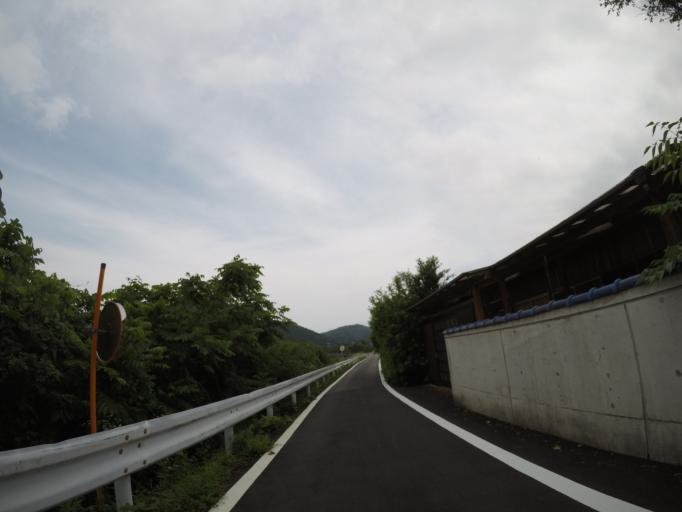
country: JP
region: Shizuoka
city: Fujinomiya
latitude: 35.2310
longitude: 138.5614
